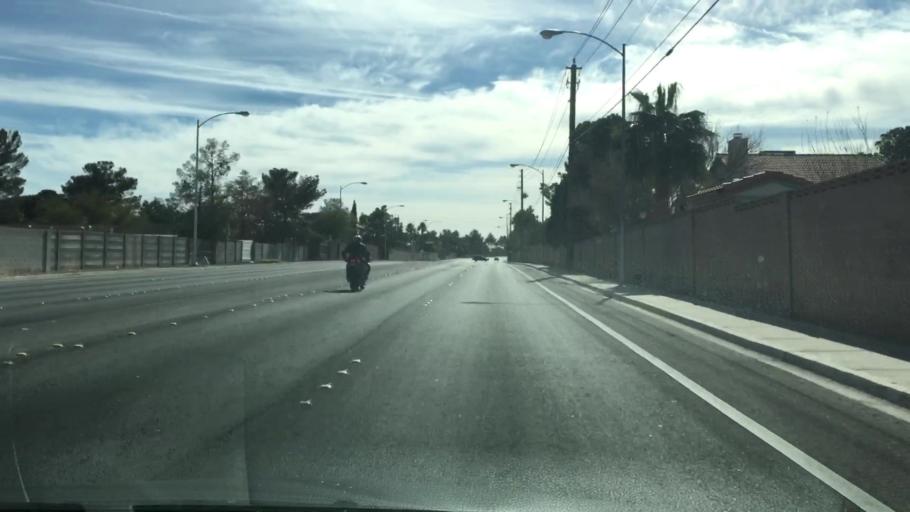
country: US
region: Nevada
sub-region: Clark County
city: Whitney
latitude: 36.0449
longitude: -115.1274
